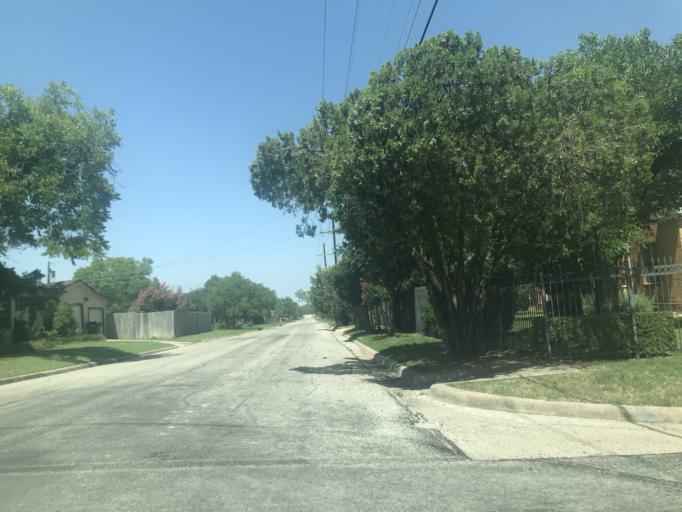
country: US
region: Texas
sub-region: Taylor County
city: Abilene
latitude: 32.4729
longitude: -99.7406
